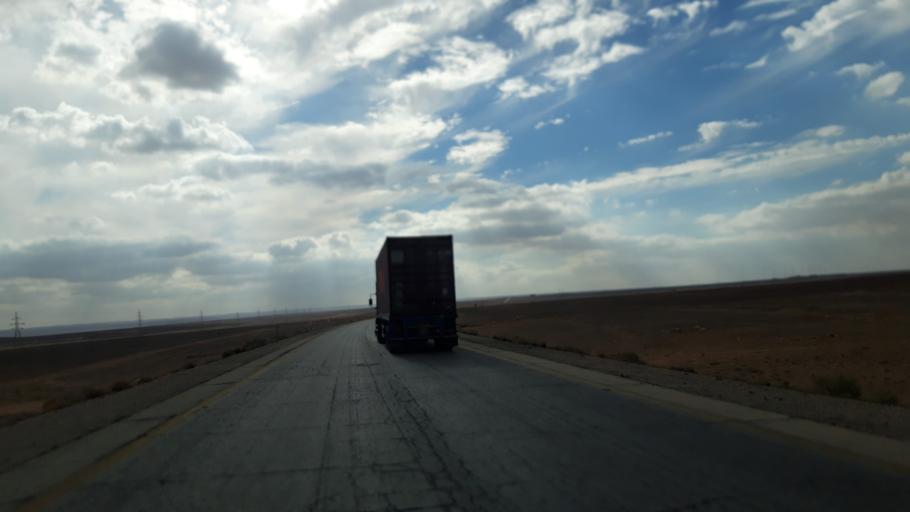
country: JO
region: Amman
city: Al Azraq ash Shamali
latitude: 31.7325
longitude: 36.5102
